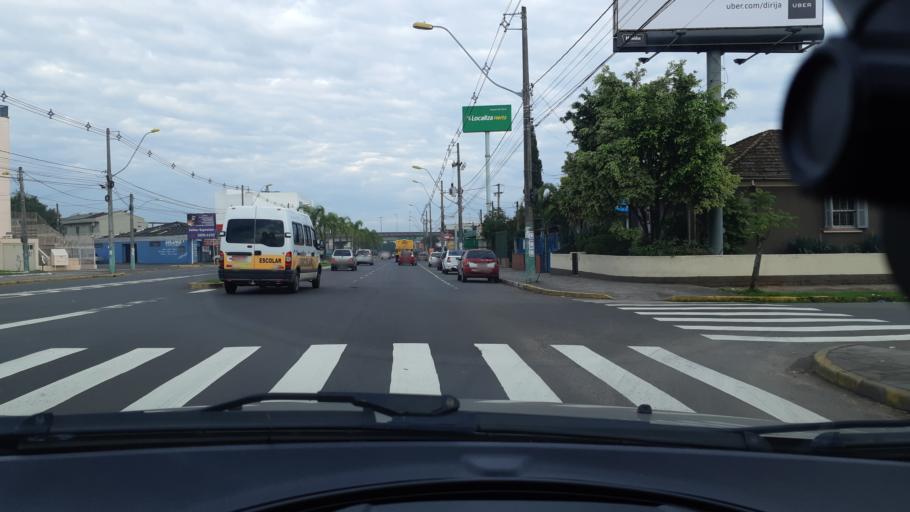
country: BR
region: Rio Grande do Sul
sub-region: Sao Leopoldo
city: Sao Leopoldo
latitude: -29.7719
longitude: -51.1514
